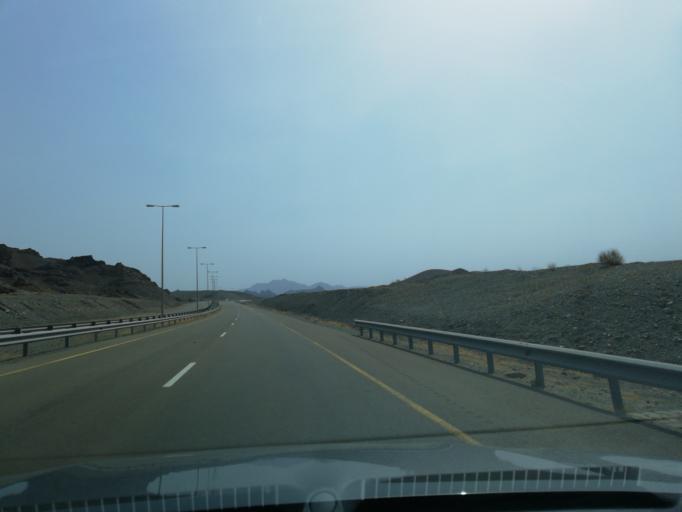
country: OM
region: Al Batinah
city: Al Liwa'
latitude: 24.2852
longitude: 56.4127
